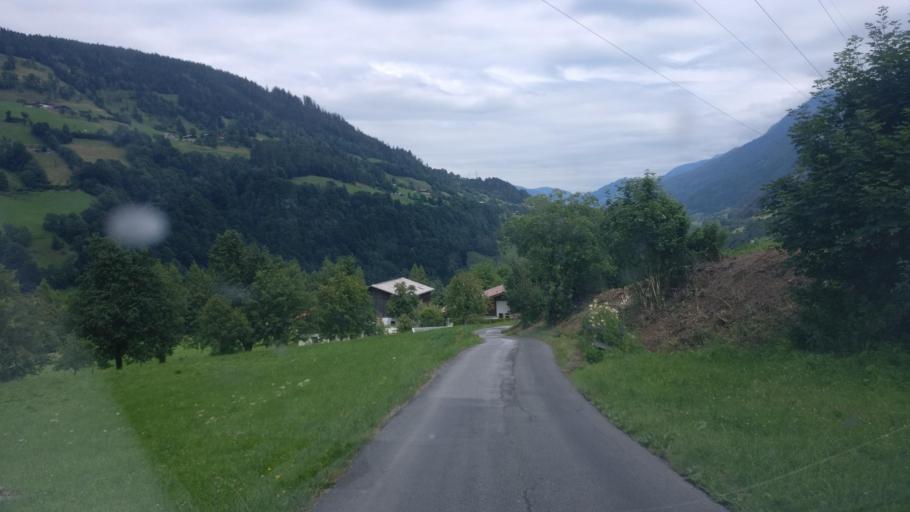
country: AT
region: Salzburg
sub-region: Politischer Bezirk Zell am See
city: Lend
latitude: 47.2943
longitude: 13.0431
